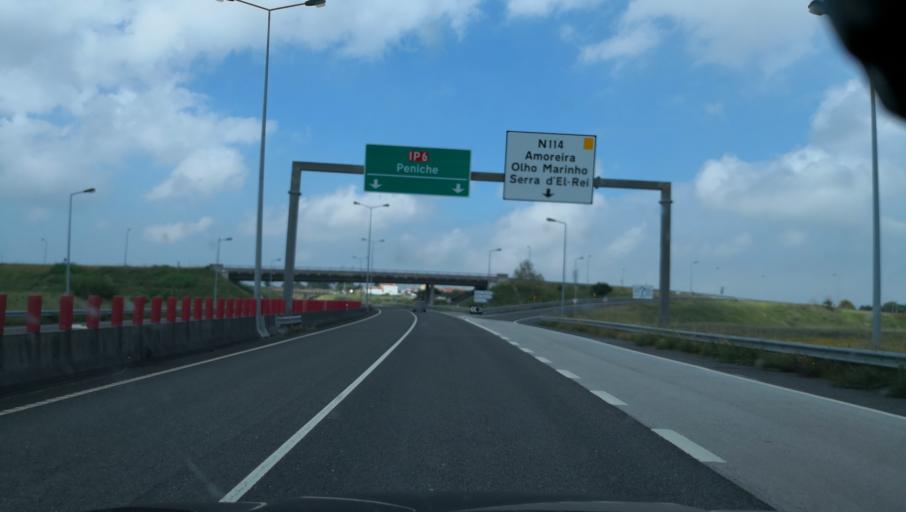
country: PT
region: Leiria
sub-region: Peniche
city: Atouguia da Baleia
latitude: 39.3315
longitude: -9.2553
